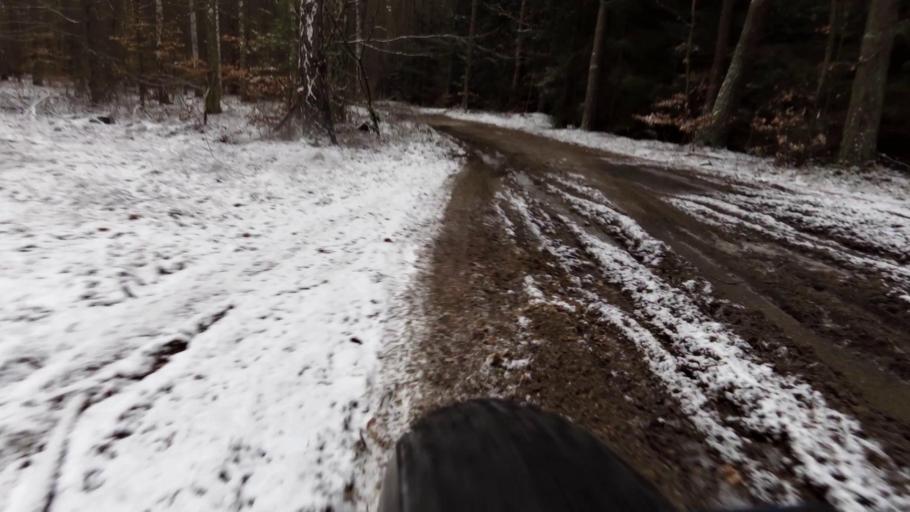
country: PL
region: West Pomeranian Voivodeship
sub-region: Powiat walecki
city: Miroslawiec
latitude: 53.3038
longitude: 16.0658
